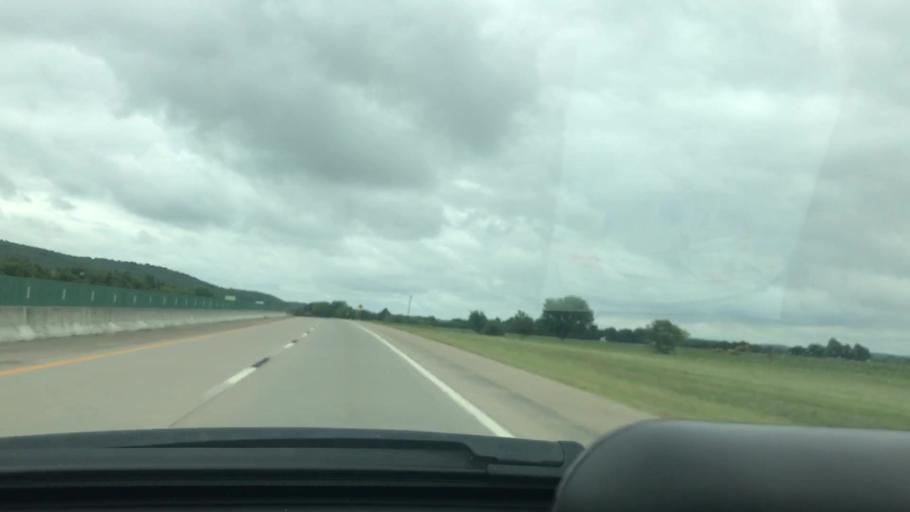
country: US
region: Oklahoma
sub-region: Pittsburg County
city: Krebs
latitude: 35.0586
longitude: -95.7065
